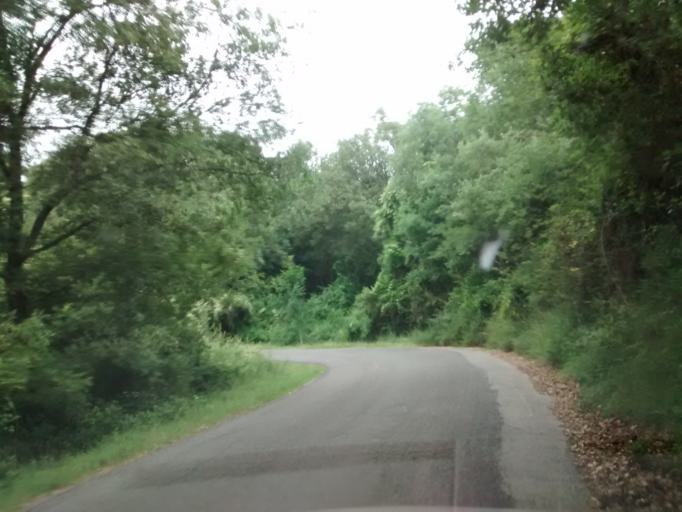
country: ES
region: Aragon
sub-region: Provincia de Huesca
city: Puertolas
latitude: 42.5412
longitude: 0.1301
